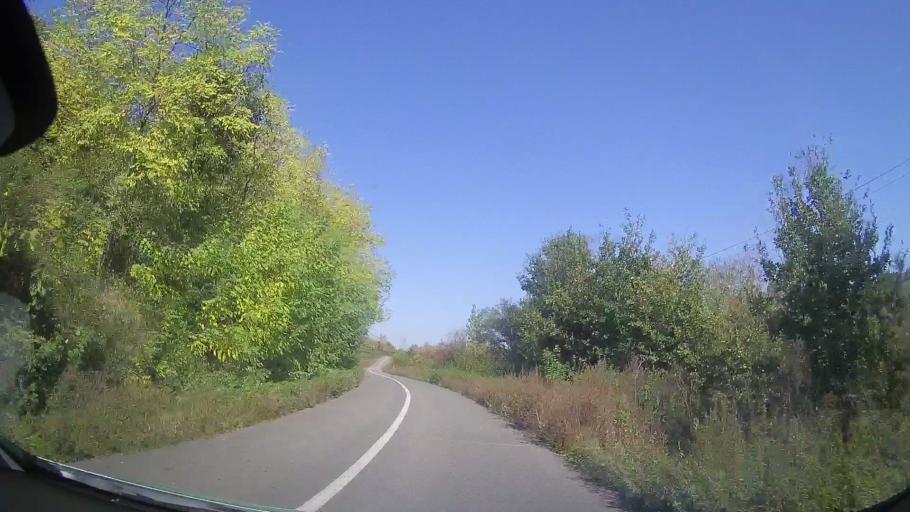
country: RO
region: Timis
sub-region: Comuna Bara
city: Bara
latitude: 45.8754
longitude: 21.8852
